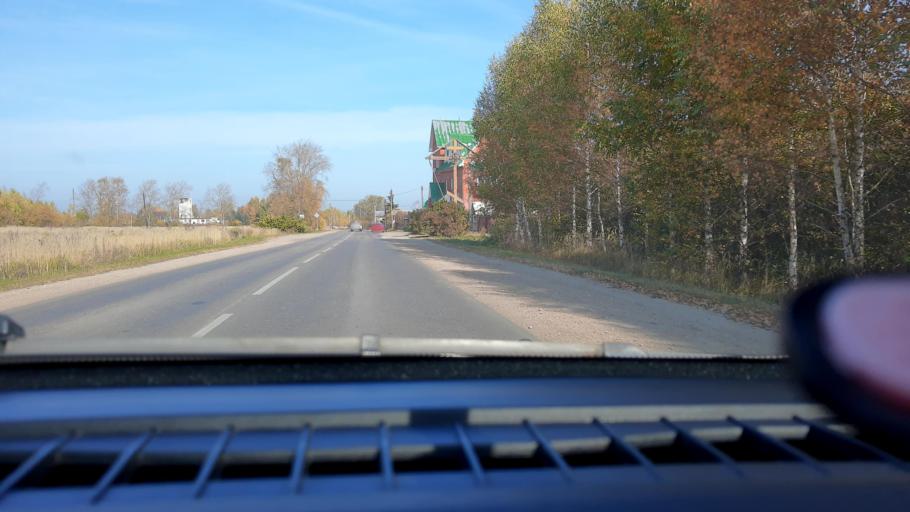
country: RU
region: Nizjnij Novgorod
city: Kstovo
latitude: 56.1499
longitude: 44.2315
